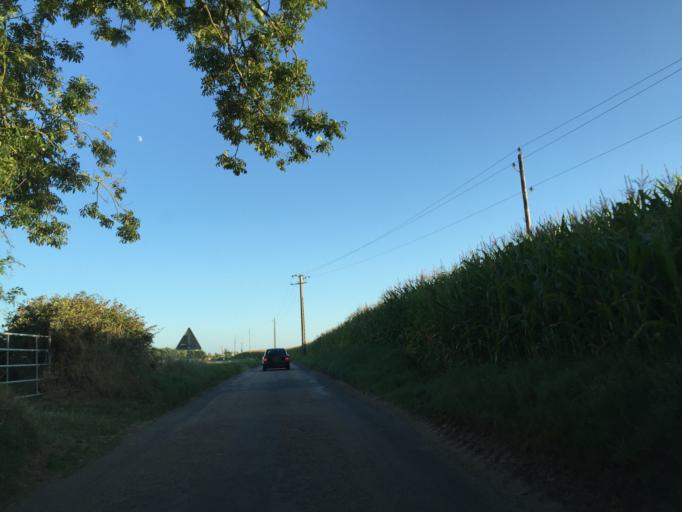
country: FR
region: Lower Normandy
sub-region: Departement du Calvados
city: Equemauville
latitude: 49.4039
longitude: 0.2047
